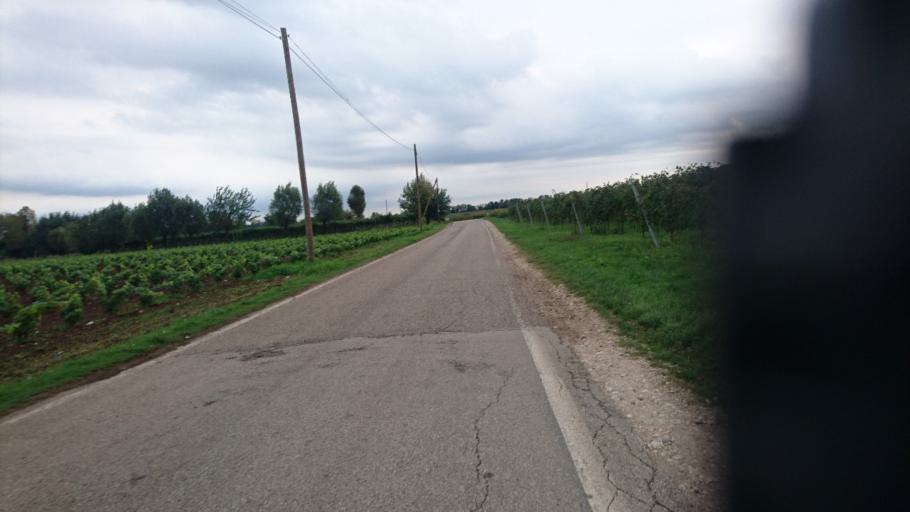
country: IT
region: Veneto
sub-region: Provincia di Vicenza
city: Gambellara
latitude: 45.4388
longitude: 11.3386
